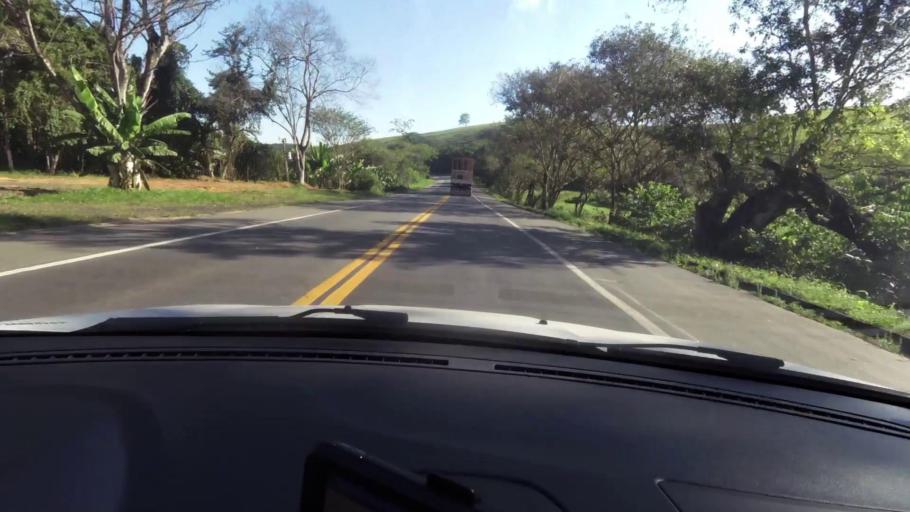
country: BR
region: Espirito Santo
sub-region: Alfredo Chaves
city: Alfredo Chaves
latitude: -20.6539
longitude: -40.6446
